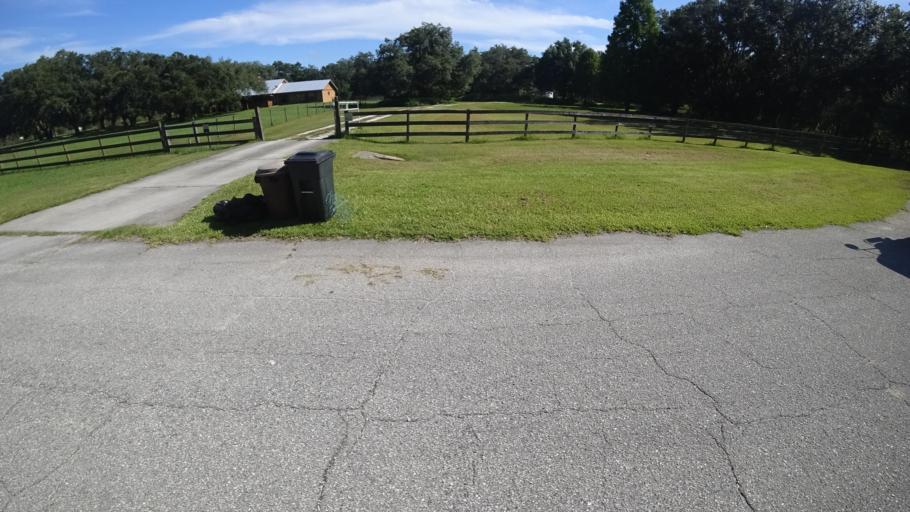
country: US
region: Florida
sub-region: Sarasota County
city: Lake Sarasota
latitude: 27.2868
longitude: -82.2273
